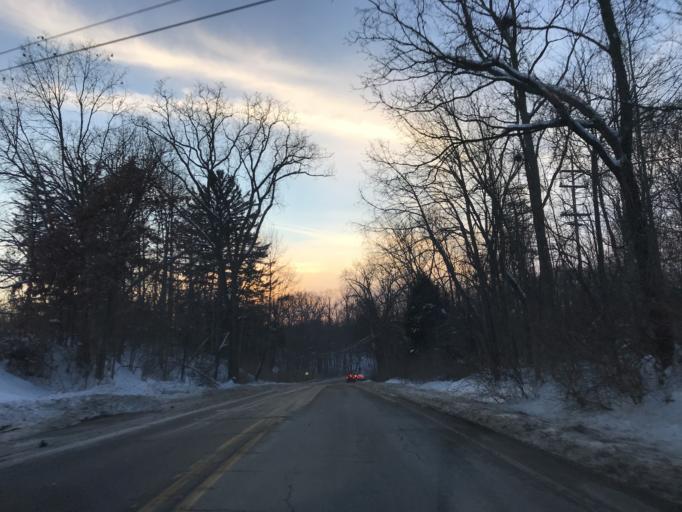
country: US
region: Michigan
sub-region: Oakland County
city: Farmington
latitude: 42.4566
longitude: -83.3118
